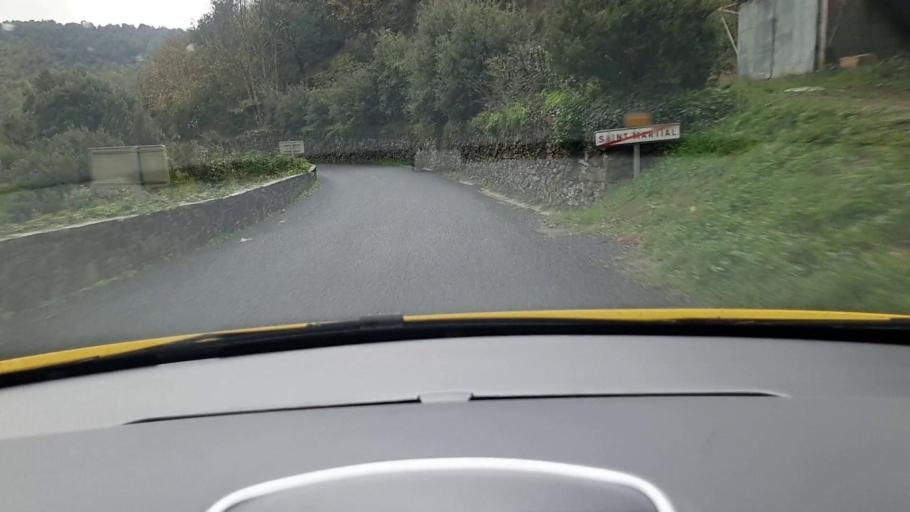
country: FR
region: Languedoc-Roussillon
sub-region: Departement du Gard
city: Sumene
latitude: 44.0333
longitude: 3.7352
